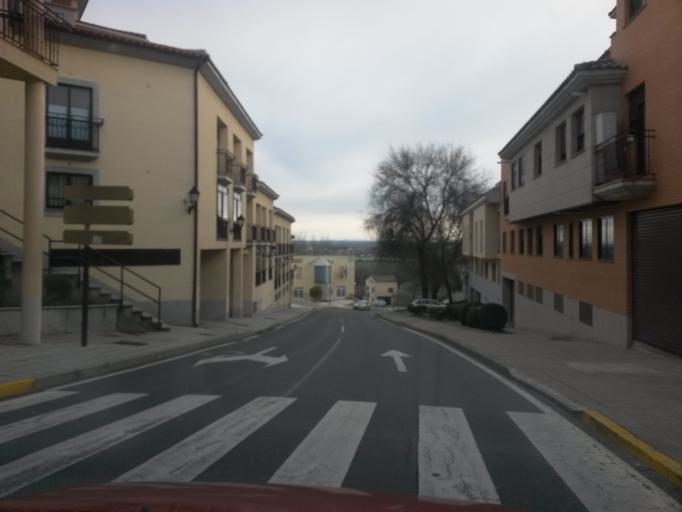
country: ES
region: Castille and Leon
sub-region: Provincia de Salamanca
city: Cabrerizos
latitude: 40.9780
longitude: -5.6101
